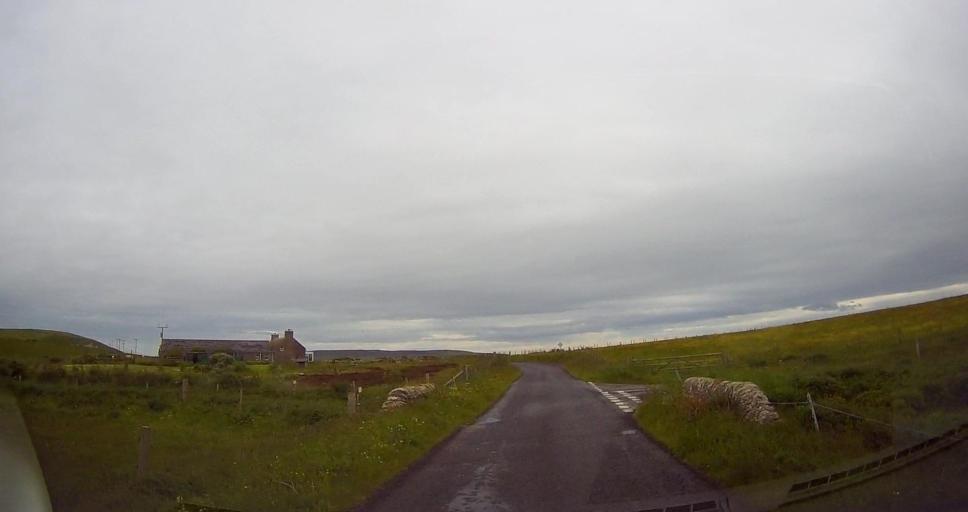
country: GB
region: Scotland
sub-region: Orkney Islands
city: Stromness
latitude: 59.1232
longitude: -3.2767
